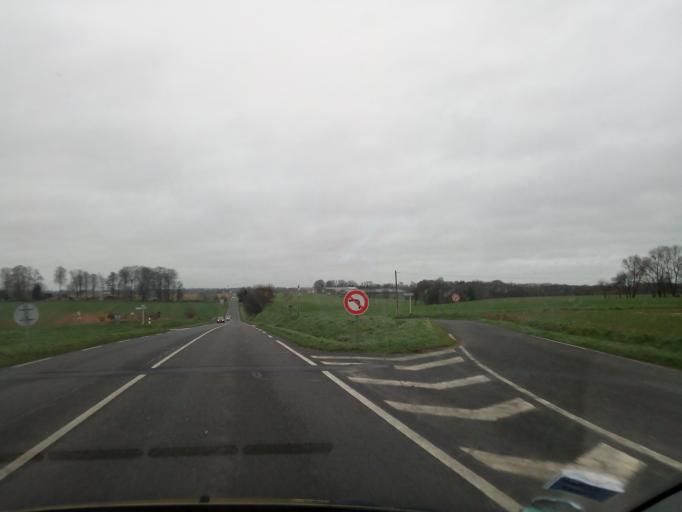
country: FR
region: Haute-Normandie
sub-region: Departement de la Seine-Maritime
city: Auzebosc
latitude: 49.5896
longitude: 0.7340
